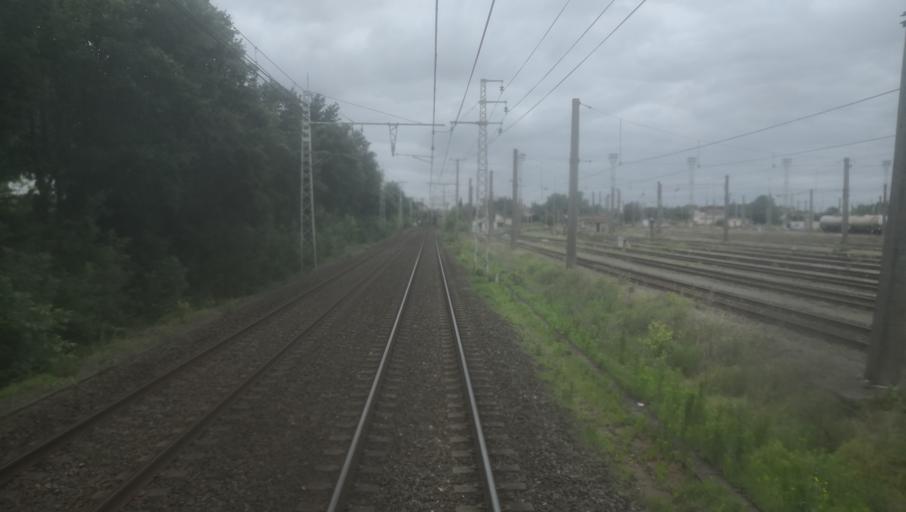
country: FR
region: Midi-Pyrenees
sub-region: Departement de la Haute-Garonne
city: Lespinasse
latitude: 43.7048
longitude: 1.3895
